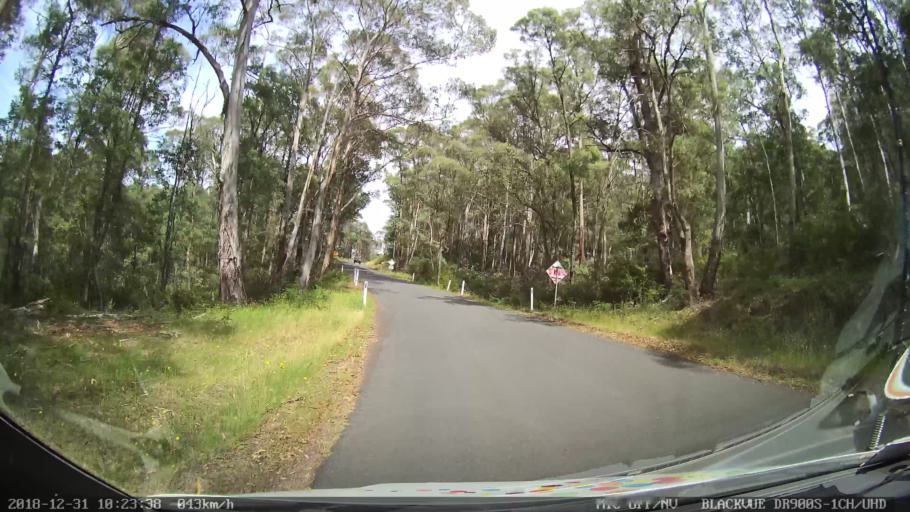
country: AU
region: New South Wales
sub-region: Snowy River
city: Jindabyne
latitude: -36.5163
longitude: 148.1442
